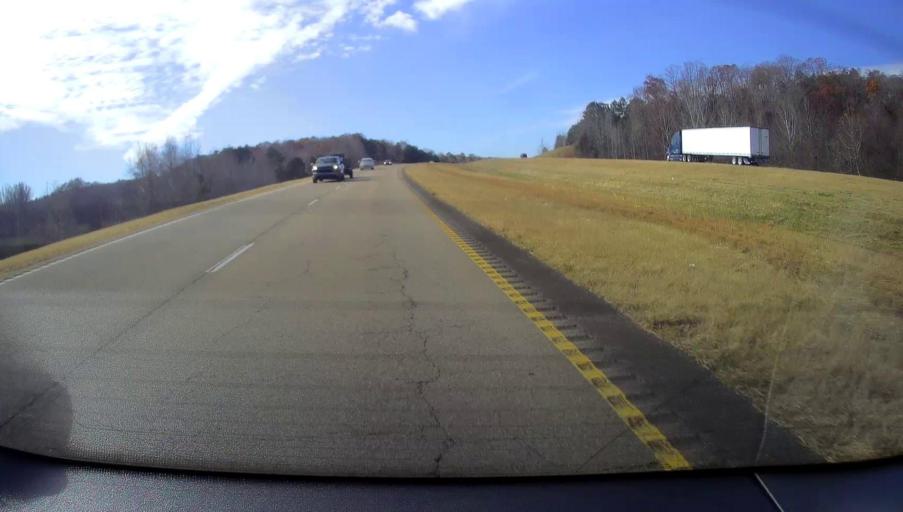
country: US
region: Mississippi
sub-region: Alcorn County
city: Corinth
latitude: 34.9321
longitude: -88.7563
